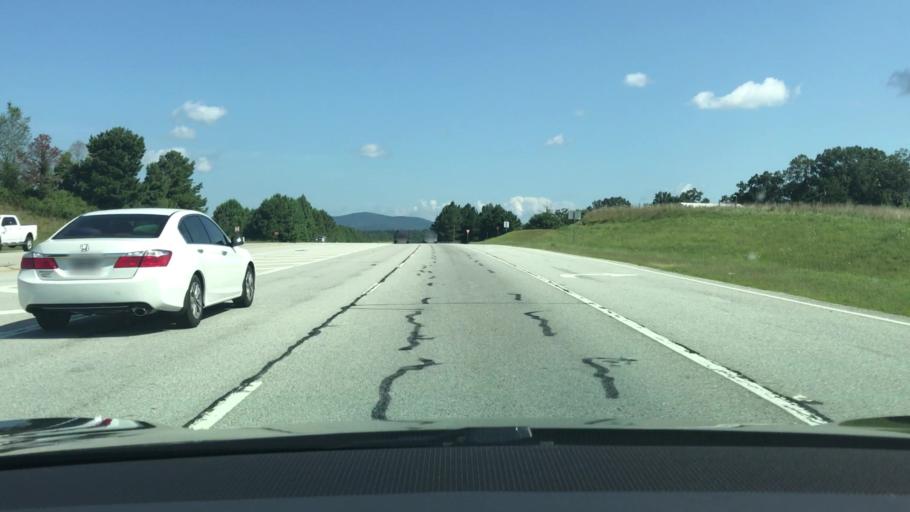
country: US
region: Georgia
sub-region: Habersham County
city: Clarkesville
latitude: 34.6259
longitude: -83.4474
